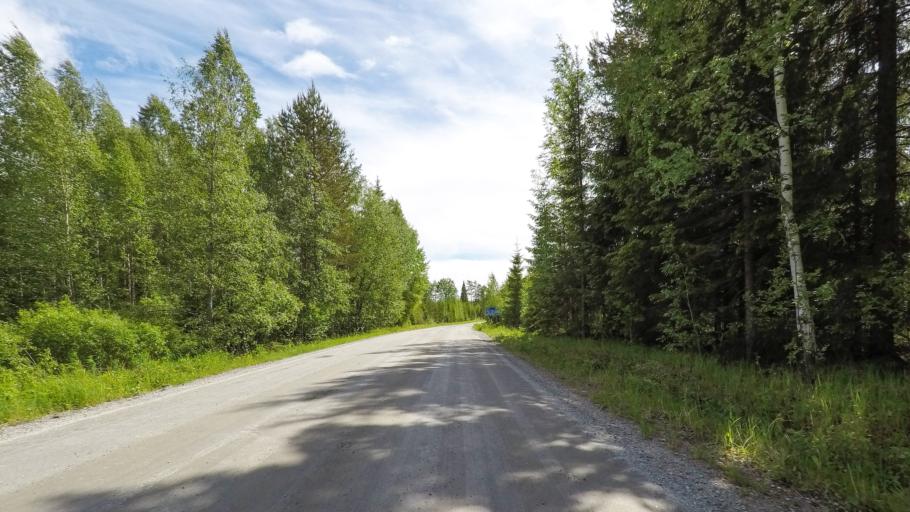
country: FI
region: Central Finland
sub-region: Jyvaeskylae
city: Hankasalmi
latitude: 62.3884
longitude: 26.6038
